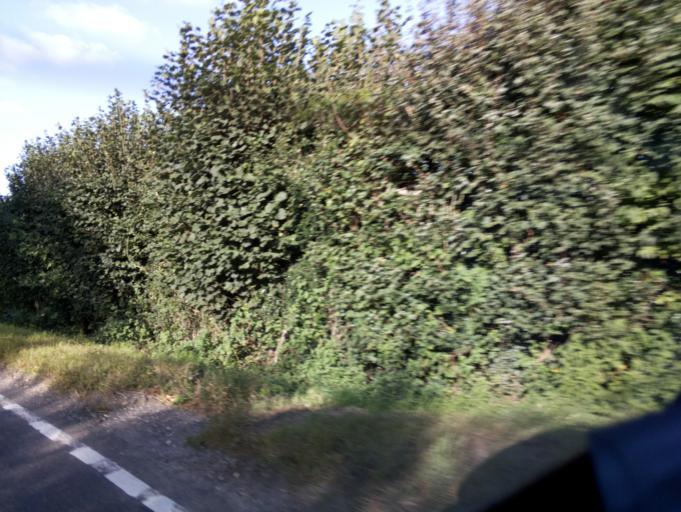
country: GB
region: England
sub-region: Hampshire
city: Alton
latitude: 51.1047
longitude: -0.9936
